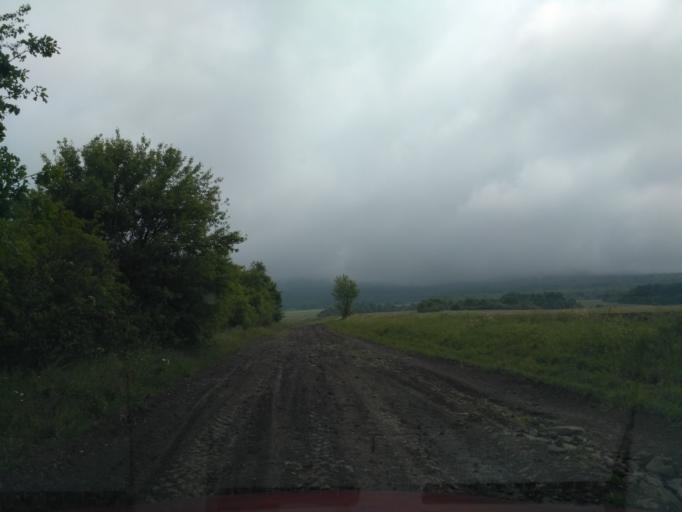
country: SK
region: Kosicky
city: Secovce
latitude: 48.7654
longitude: 21.4944
